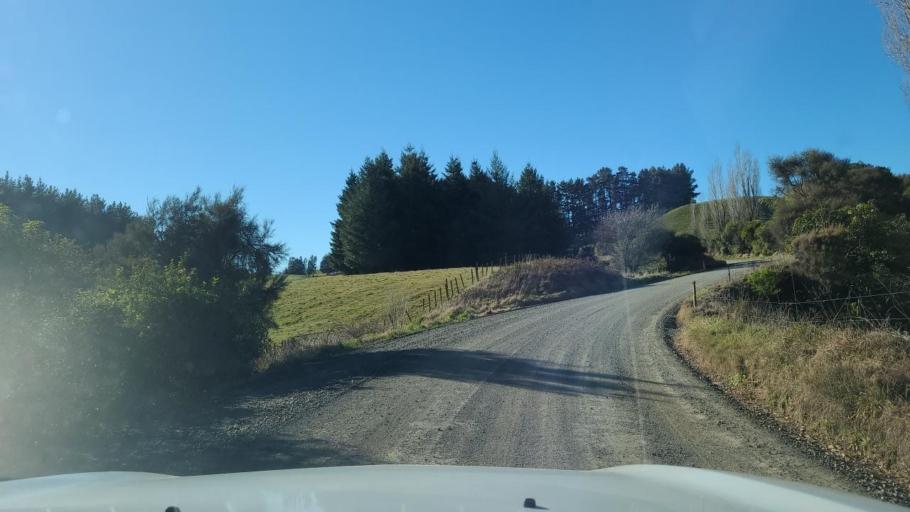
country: NZ
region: Hawke's Bay
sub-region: Napier City
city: Taradale
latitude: -39.3761
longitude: 176.5760
